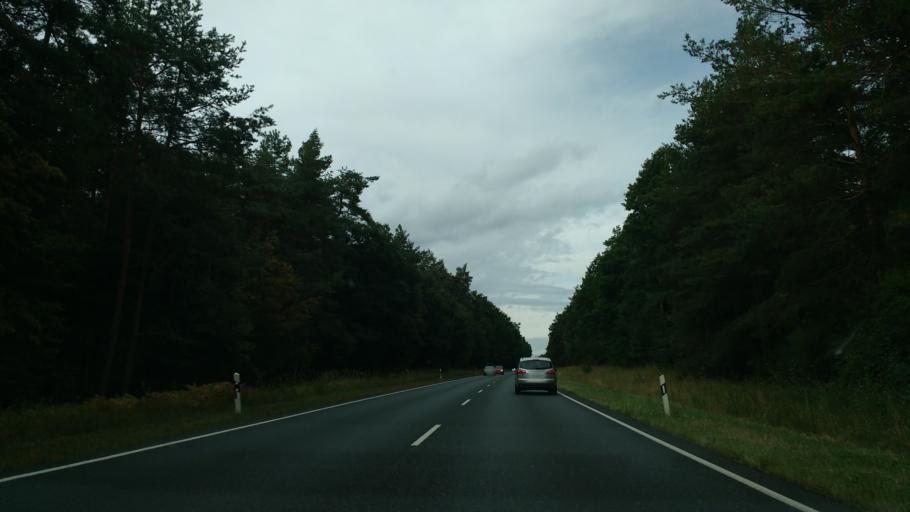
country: DE
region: Bavaria
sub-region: Regierungsbezirk Unterfranken
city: Schwebheim
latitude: 49.9984
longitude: 10.2381
